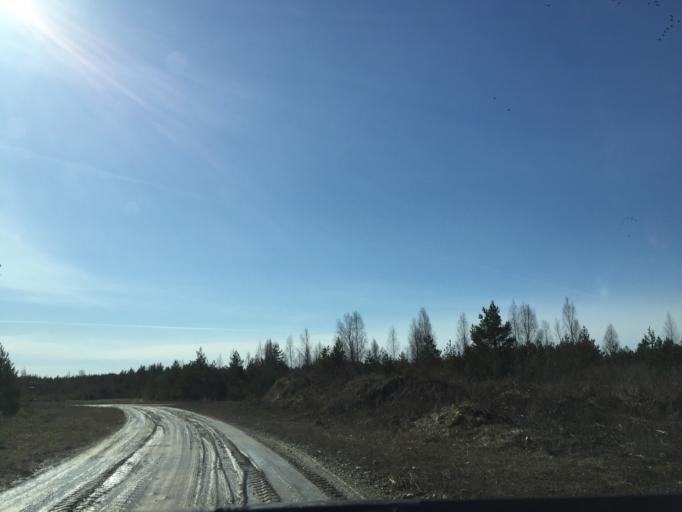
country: EE
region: Laeaene
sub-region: Haapsalu linn
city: Haapsalu
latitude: 58.6325
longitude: 23.5252
